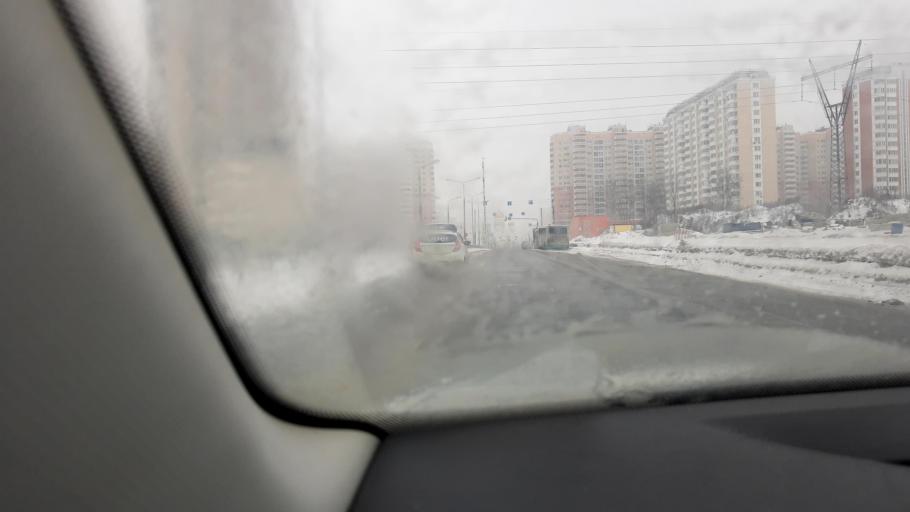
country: RU
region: Moscow
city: Nekrasovka
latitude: 55.7094
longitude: 37.9344
